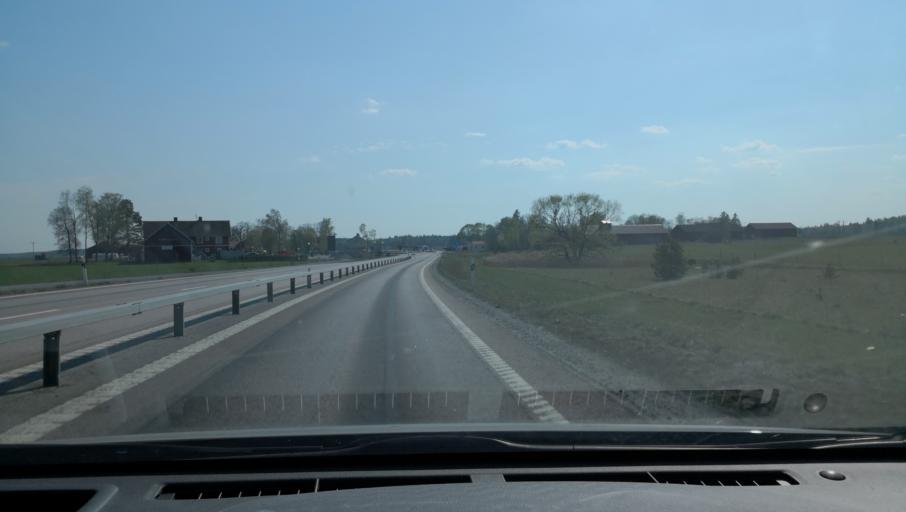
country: SE
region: Vaestmanland
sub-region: Sala Kommun
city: Sala
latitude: 59.8608
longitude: 16.5397
